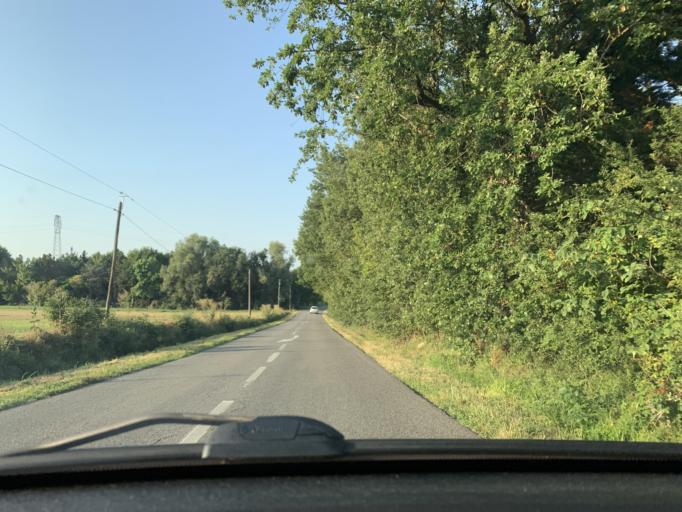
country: FR
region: Midi-Pyrenees
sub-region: Departement de la Haute-Garonne
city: Auzielle
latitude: 43.5333
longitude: 1.5686
